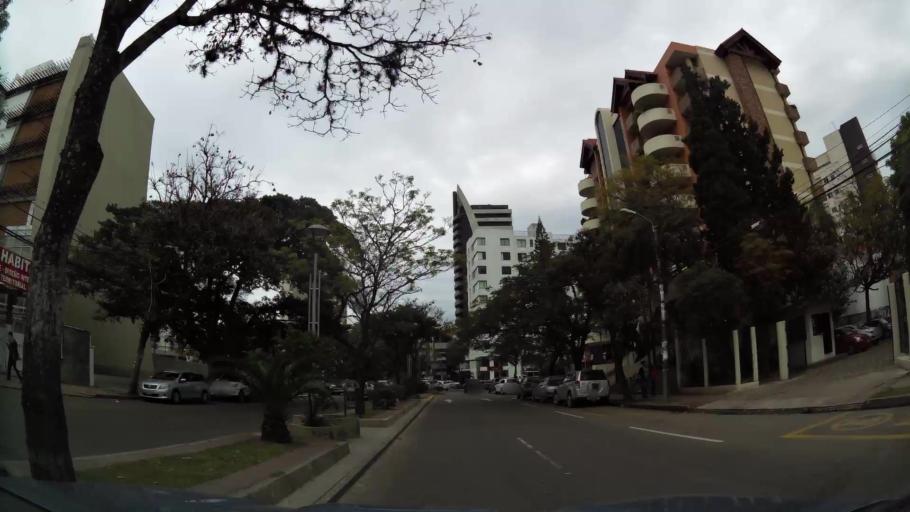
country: BO
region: Santa Cruz
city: Santa Cruz de la Sierra
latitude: -17.7694
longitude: -63.1919
